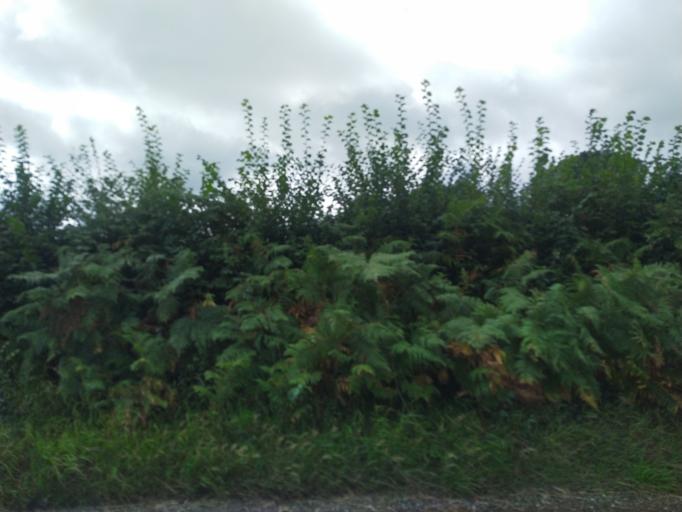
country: GB
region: England
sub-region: Dorset
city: Lytchett Matravers
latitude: 50.7522
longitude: -2.1253
